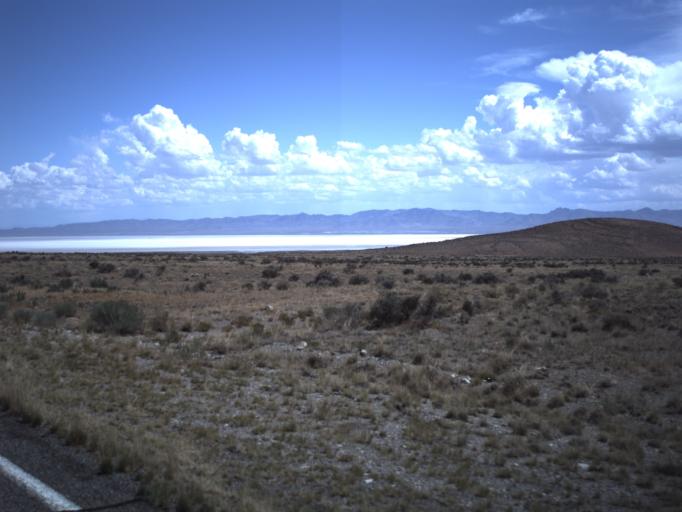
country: US
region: Utah
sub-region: Beaver County
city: Milford
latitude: 39.0458
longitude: -113.2856
